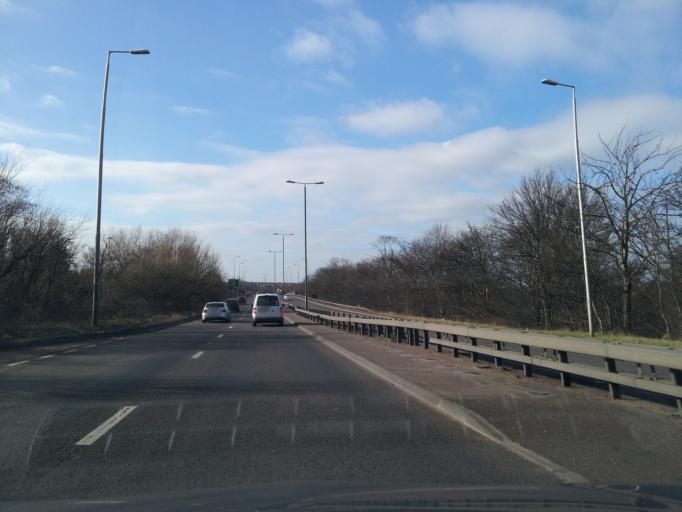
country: GB
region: England
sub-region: Derbyshire
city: Long Eaton
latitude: 52.9196
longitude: -1.2764
